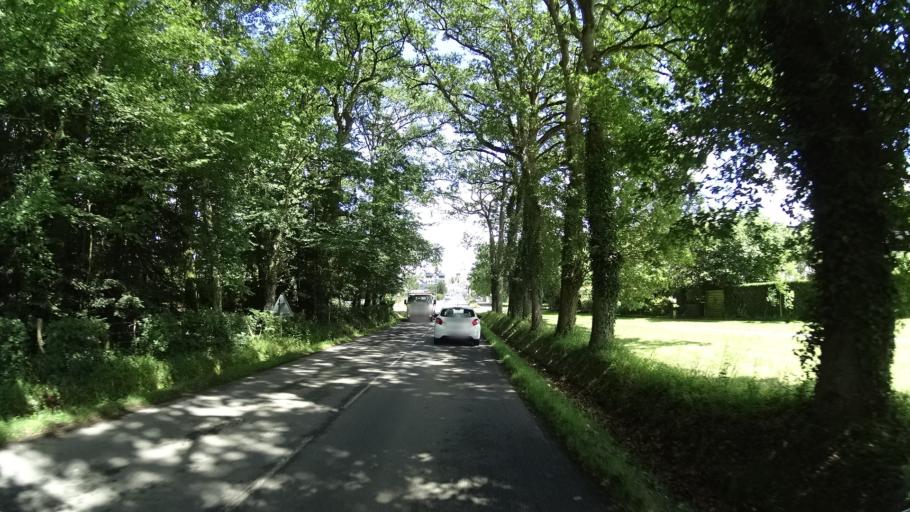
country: FR
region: Brittany
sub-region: Departement d'Ille-et-Vilaine
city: Saint-Gilles
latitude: 48.1499
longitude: -1.8305
